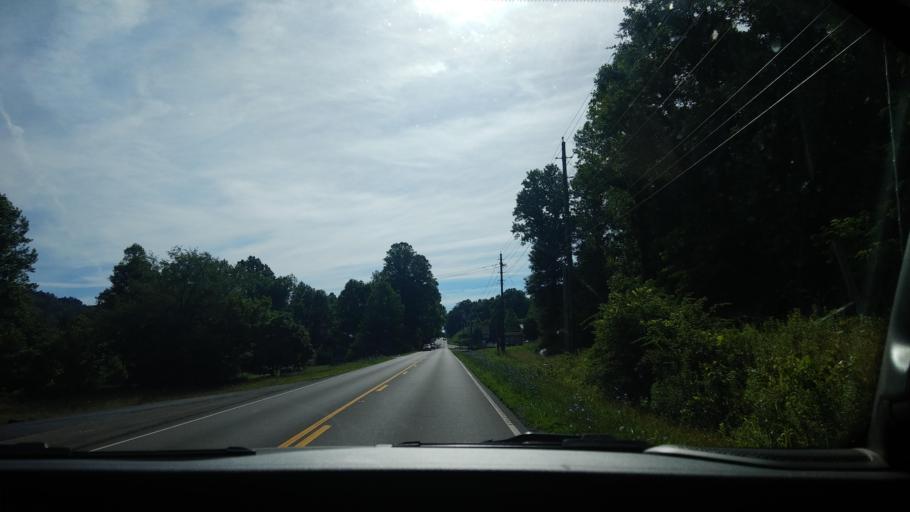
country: US
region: Tennessee
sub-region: Sevier County
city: Gatlinburg
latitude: 35.7579
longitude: -83.3598
